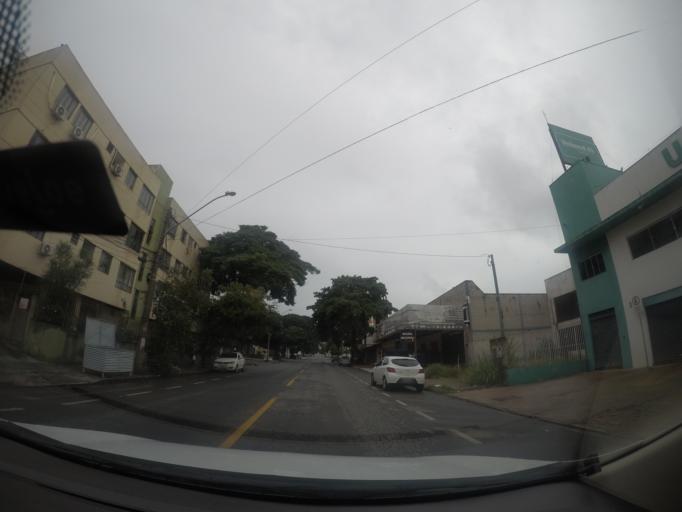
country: BR
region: Goias
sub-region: Goiania
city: Goiania
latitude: -16.7092
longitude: -49.2839
